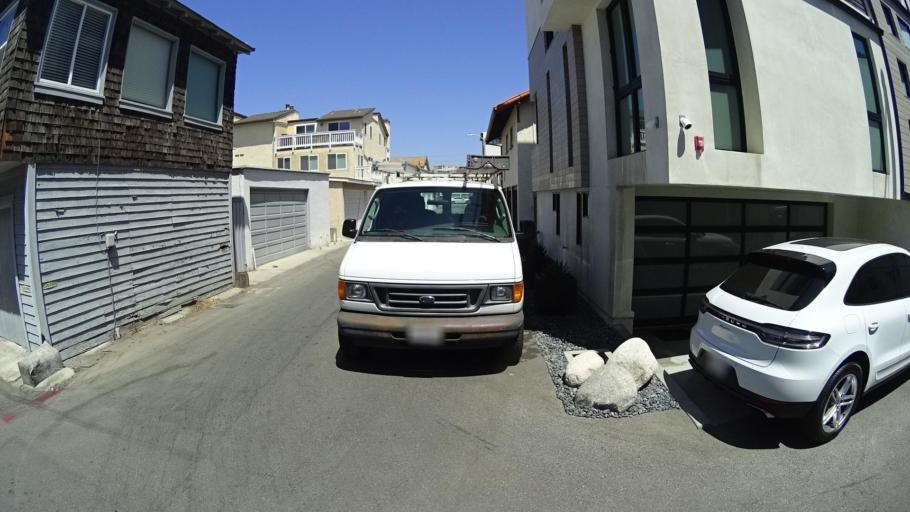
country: US
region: California
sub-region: Los Angeles County
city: Hermosa Beach
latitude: 33.8580
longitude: -118.3999
